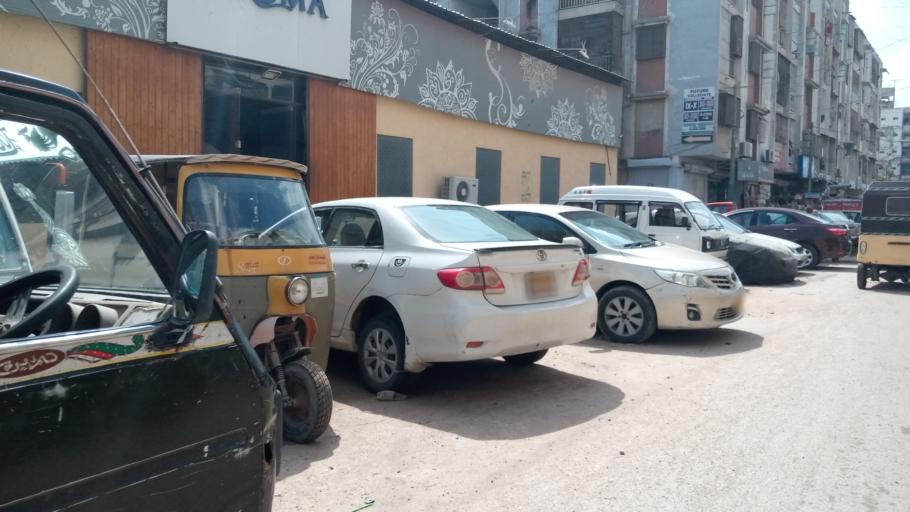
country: PK
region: Sindh
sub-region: Karachi District
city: Karachi
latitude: 24.9274
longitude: 67.0678
